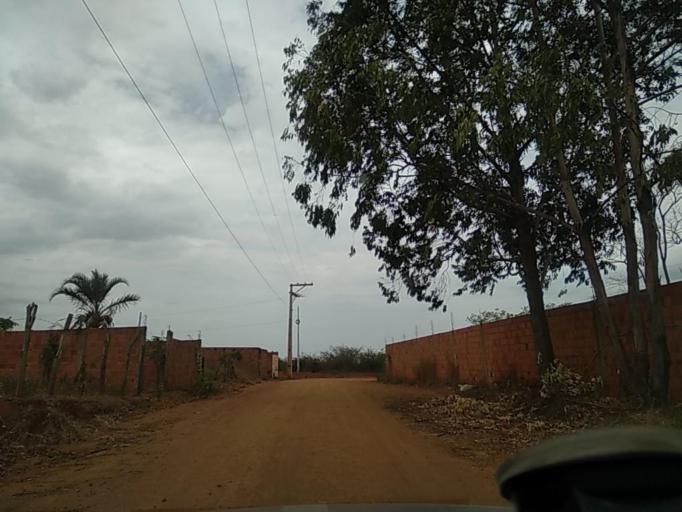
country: BR
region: Bahia
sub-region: Caetite
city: Caetite
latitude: -14.0465
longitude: -42.4738
